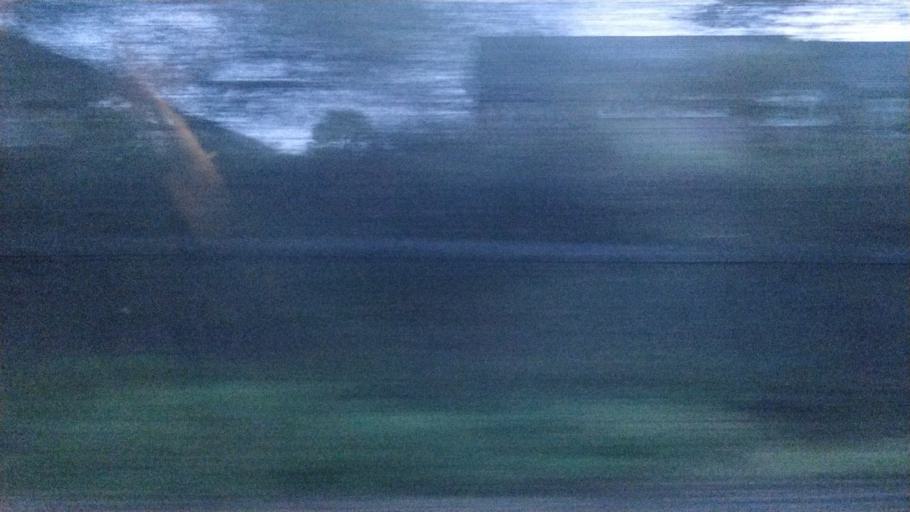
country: GB
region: England
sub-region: Borough of Bolton
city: Westhoughton
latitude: 53.5418
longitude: -2.5283
